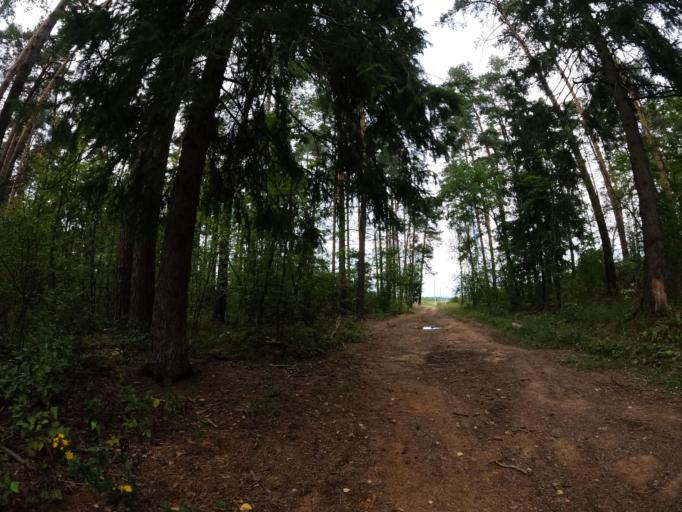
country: RU
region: Moskovskaya
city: Rodniki
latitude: 55.6682
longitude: 38.0785
